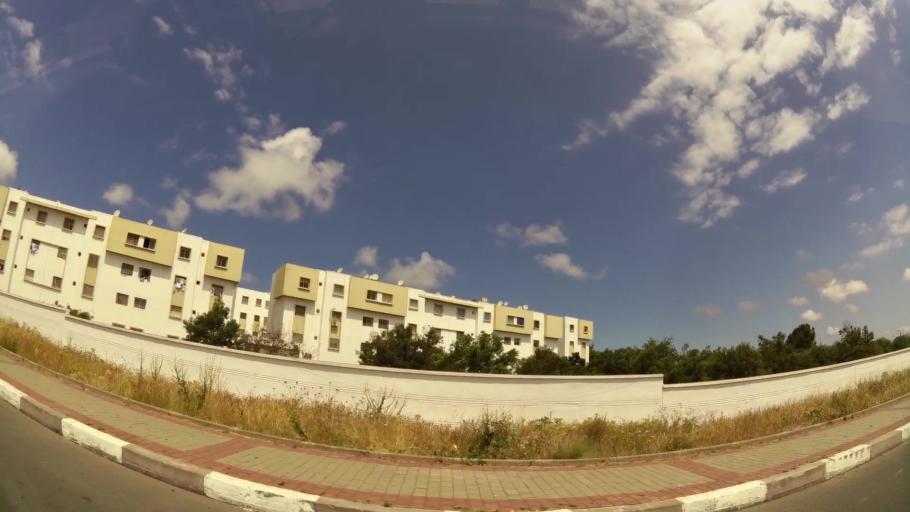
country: MA
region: Gharb-Chrarda-Beni Hssen
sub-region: Kenitra Province
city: Kenitra
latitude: 34.2762
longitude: -6.6103
